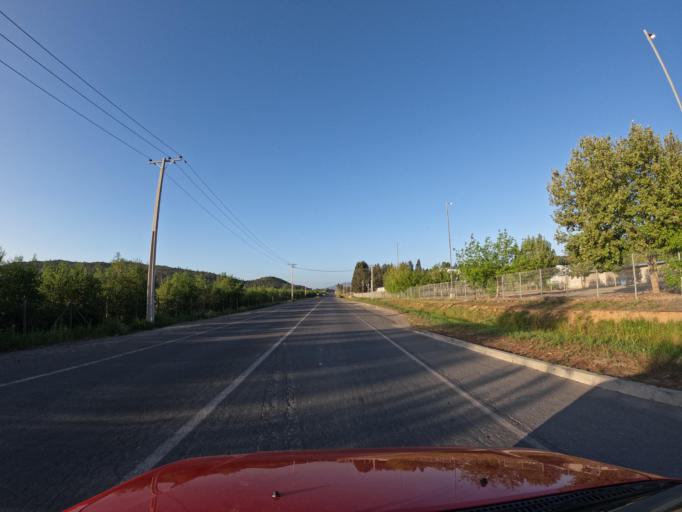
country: CL
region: O'Higgins
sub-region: Provincia de Colchagua
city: Santa Cruz
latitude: -34.3254
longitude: -71.3924
